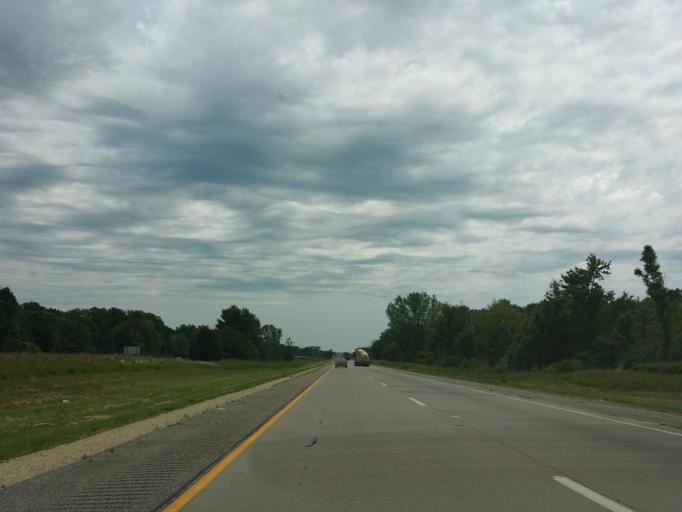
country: US
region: Wisconsin
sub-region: Juneau County
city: Mauston
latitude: 43.7307
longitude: -89.9163
